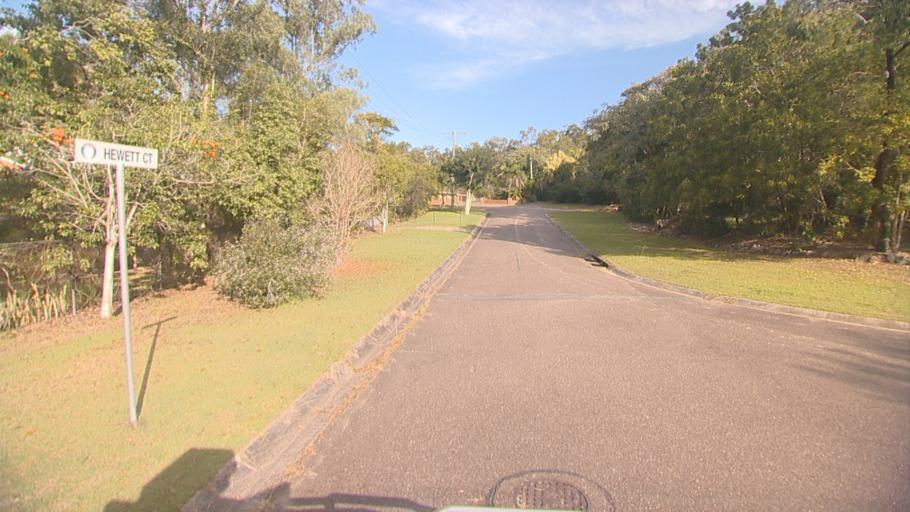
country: AU
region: Queensland
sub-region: Logan
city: Windaroo
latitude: -27.7587
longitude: 153.1965
